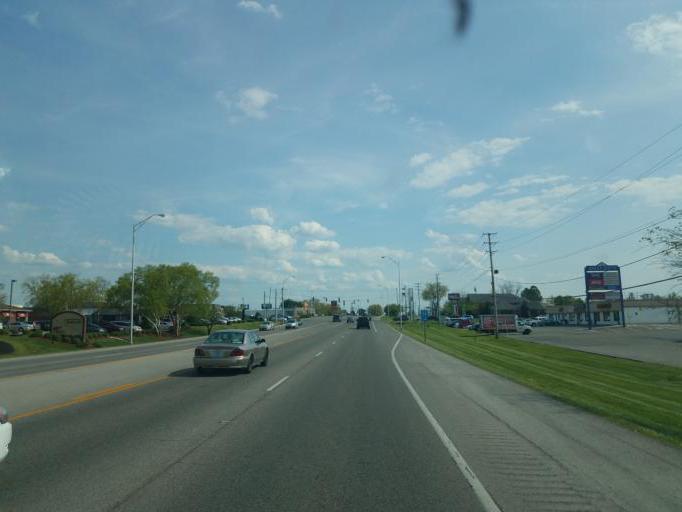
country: US
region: Kentucky
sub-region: Warren County
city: Bowling Green
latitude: 36.9675
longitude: -86.4330
